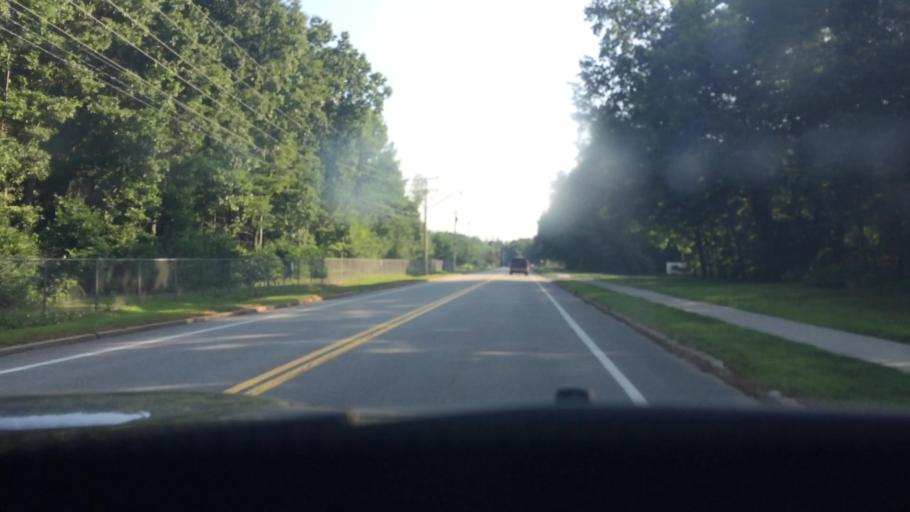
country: US
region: Maine
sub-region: York County
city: South Eliot
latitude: 43.0909
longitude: -70.8129
